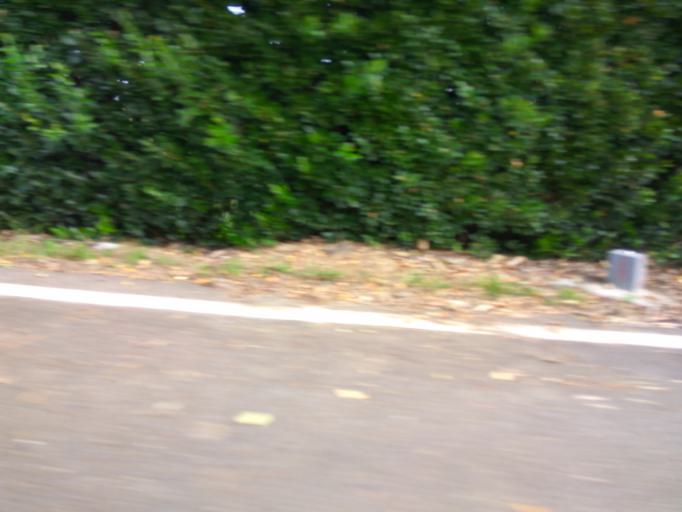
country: TW
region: Taiwan
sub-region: Hsinchu
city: Zhubei
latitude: 24.9507
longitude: 121.0005
